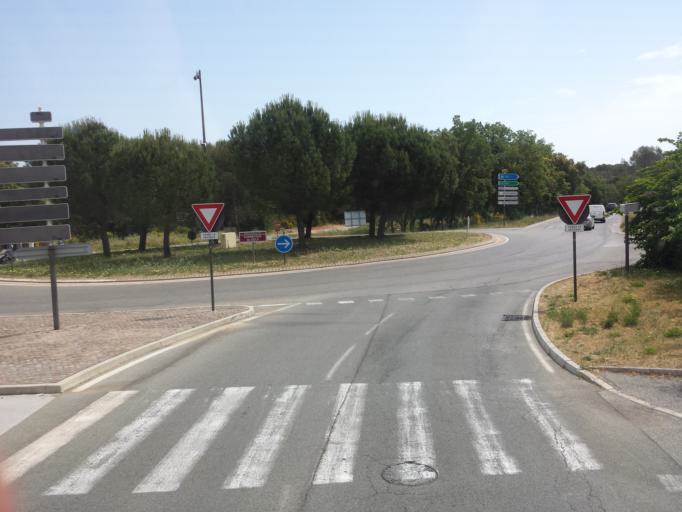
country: FR
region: Provence-Alpes-Cote d'Azur
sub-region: Departement des Alpes-Maritimes
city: Biot
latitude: 43.6172
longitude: 7.0702
